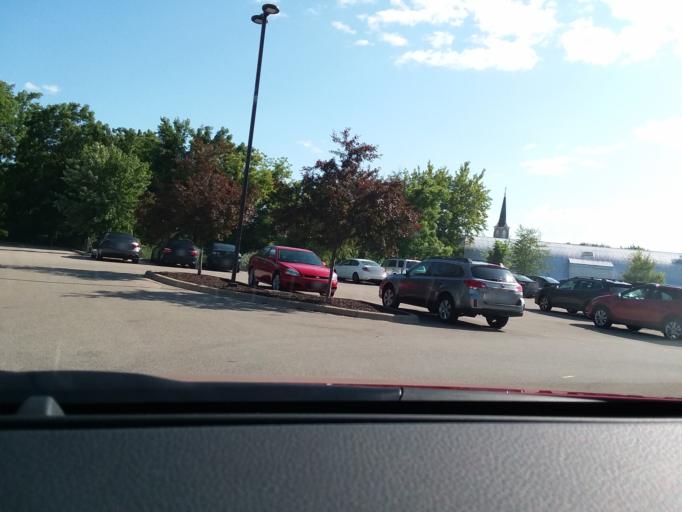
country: US
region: Wisconsin
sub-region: Dane County
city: Waunakee
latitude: 43.1915
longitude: -89.4530
